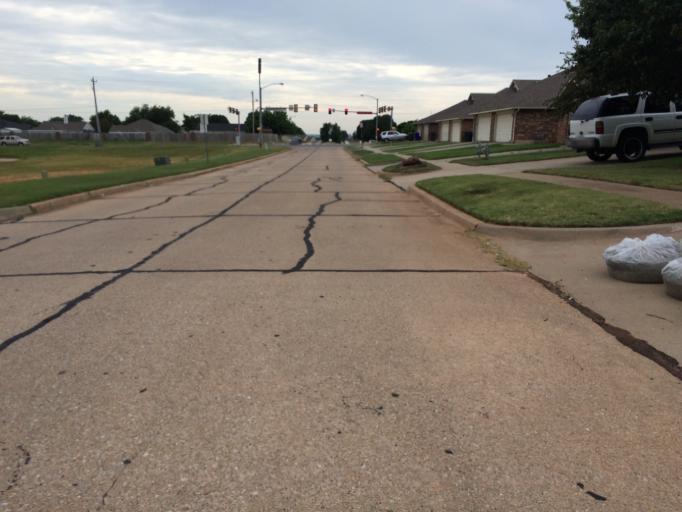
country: US
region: Oklahoma
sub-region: Cleveland County
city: Hall Park
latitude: 35.2541
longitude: -97.4223
